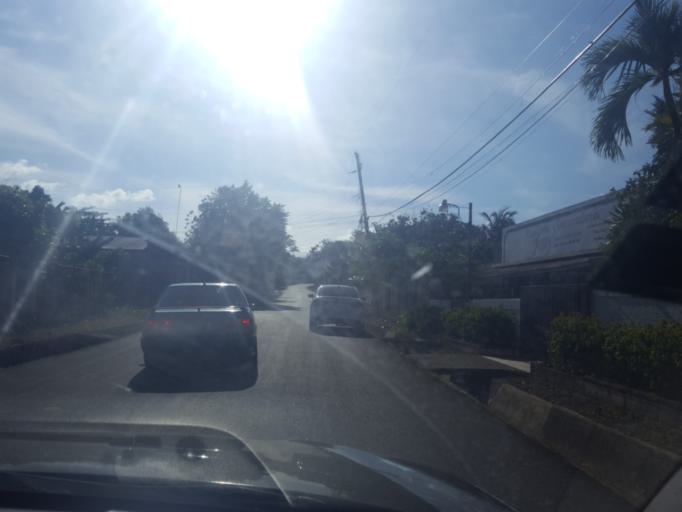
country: DO
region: La Vega
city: Rio Verde Arriba
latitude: 19.3466
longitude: -70.6228
